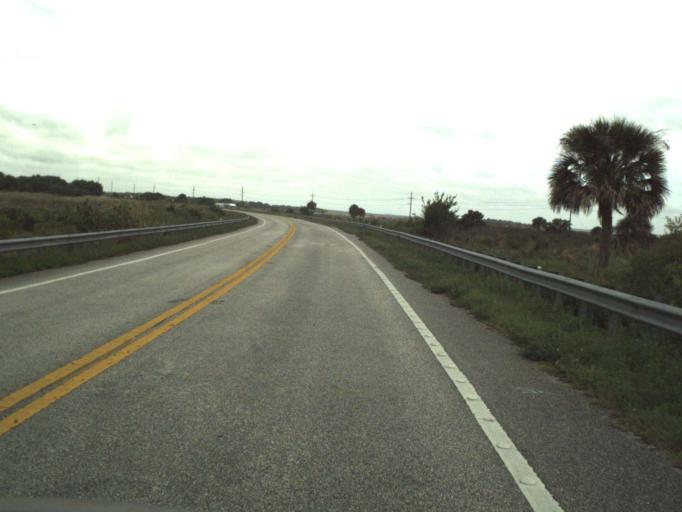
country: US
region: Florida
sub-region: Seminole County
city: Geneva
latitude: 28.7118
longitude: -81.0248
